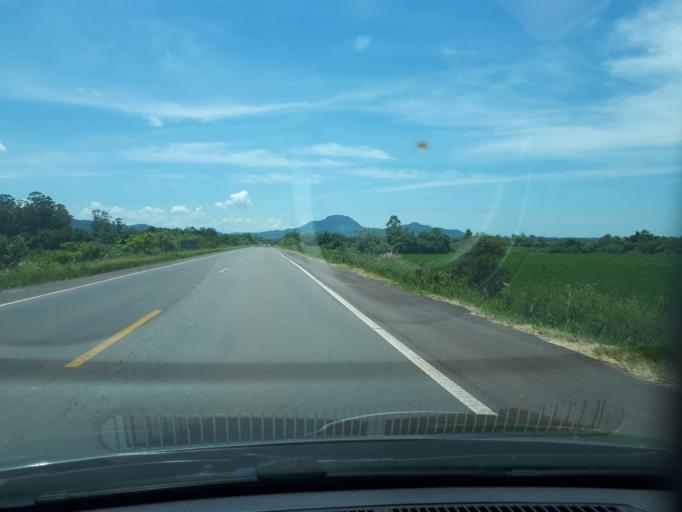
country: BR
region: Rio Grande do Sul
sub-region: Candelaria
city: Candelaria
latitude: -29.7284
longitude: -52.9384
